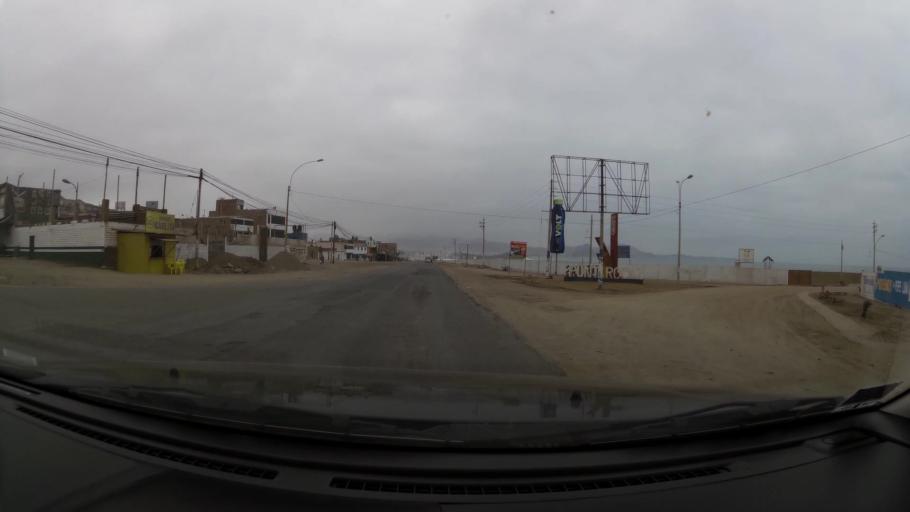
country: PE
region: Lima
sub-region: Lima
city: Punta Hermosa
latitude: -12.3509
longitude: -76.8101
